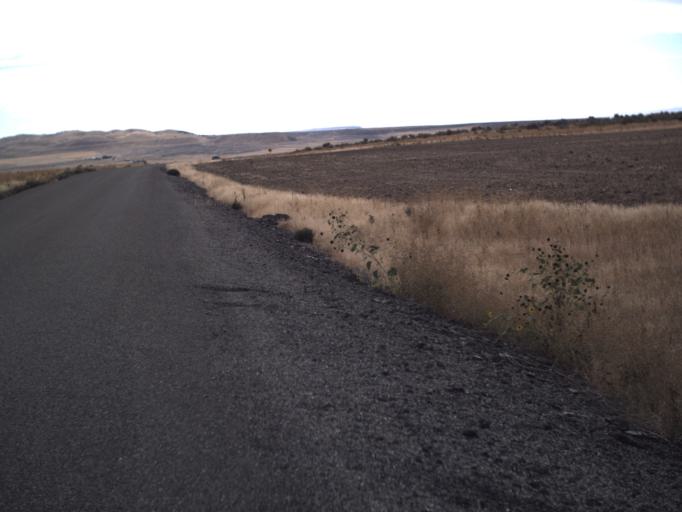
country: US
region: Idaho
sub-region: Oneida County
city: Malad City
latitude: 41.8939
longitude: -112.5755
